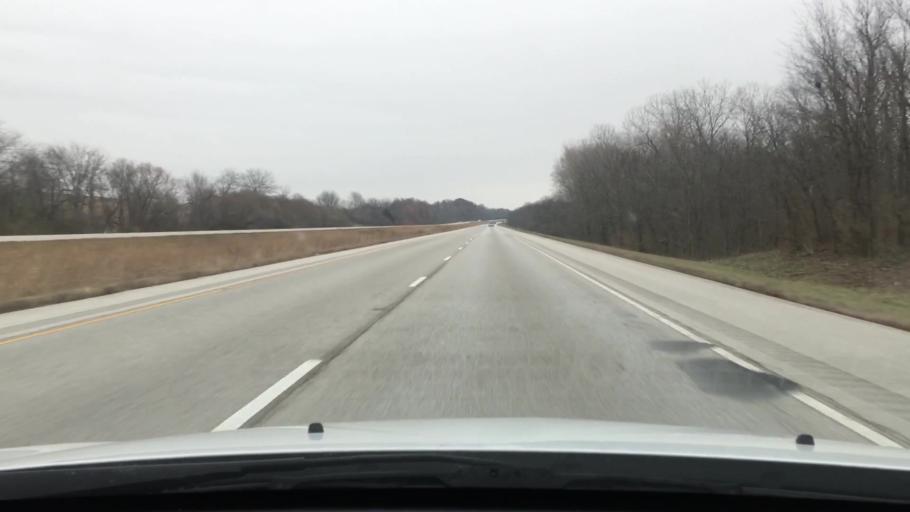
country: US
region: Illinois
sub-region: Scott County
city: Winchester
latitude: 39.6812
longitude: -90.4062
